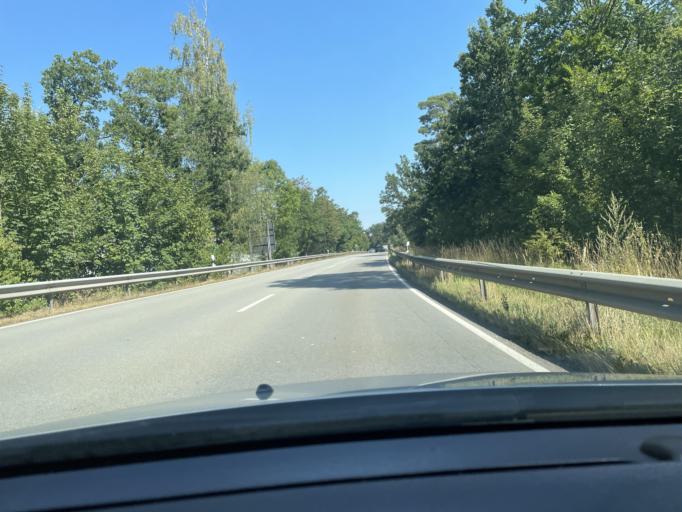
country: DE
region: Baden-Wuerttemberg
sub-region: Karlsruhe Region
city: Rheinmuenster
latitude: 48.7629
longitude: 8.0169
